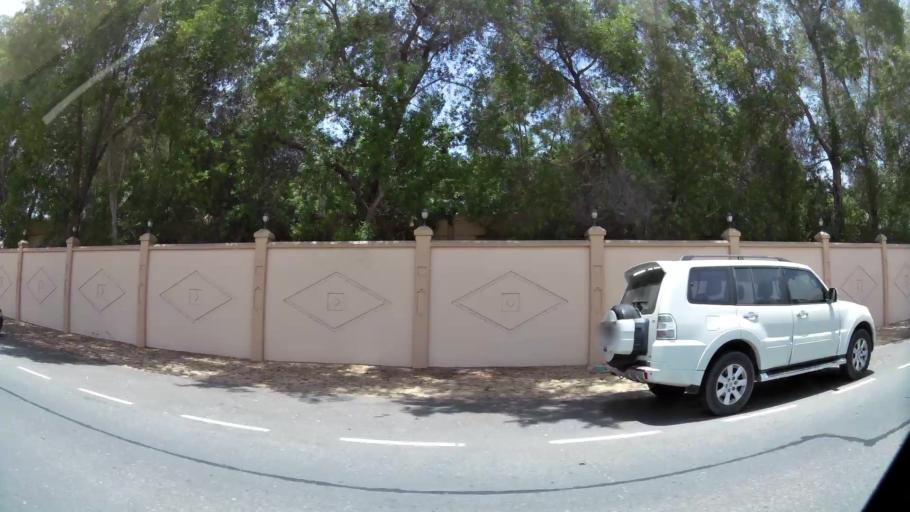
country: AE
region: Dubai
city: Dubai
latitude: 25.1738
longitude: 55.2417
